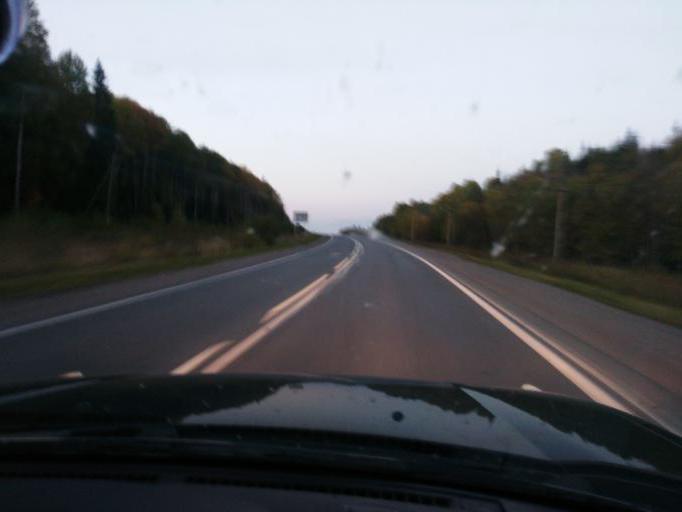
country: RU
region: Perm
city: Verkhnechusovskiye Gorodki
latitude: 58.2280
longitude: 57.2053
